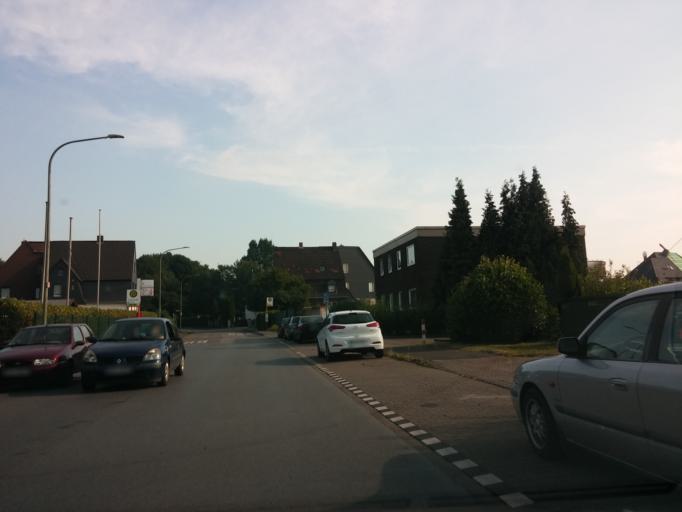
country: DE
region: North Rhine-Westphalia
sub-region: Regierungsbezirk Munster
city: Bottrop
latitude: 51.5170
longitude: 6.9524
